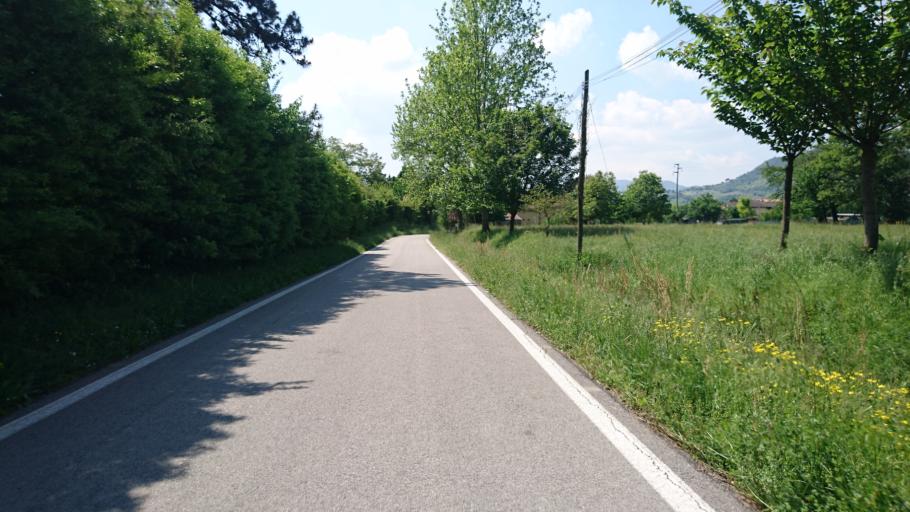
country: IT
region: Veneto
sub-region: Provincia di Padova
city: San Biagio
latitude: 45.3707
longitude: 11.7478
